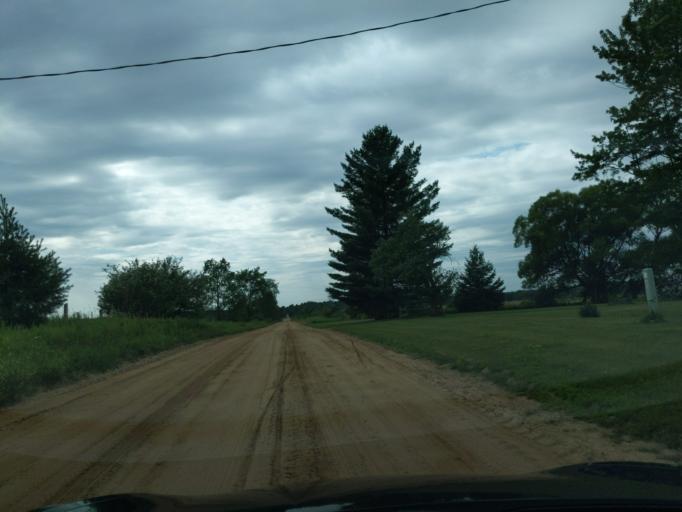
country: US
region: Michigan
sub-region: Clare County
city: Harrison
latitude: 44.0025
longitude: -84.9900
